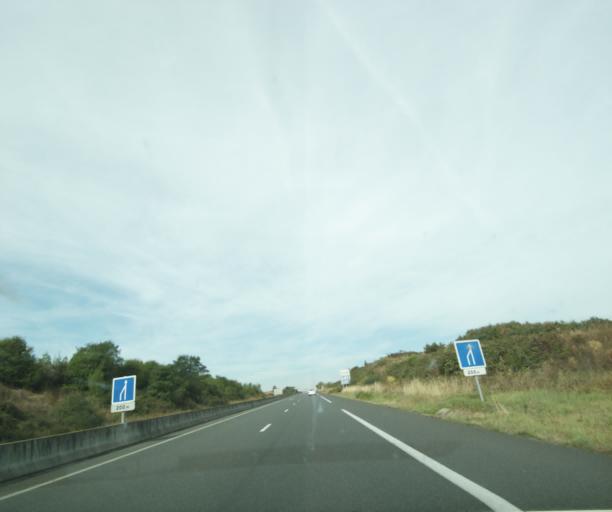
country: FR
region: Auvergne
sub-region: Departement de l'Allier
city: Lapalisse
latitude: 46.2379
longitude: 3.6253
